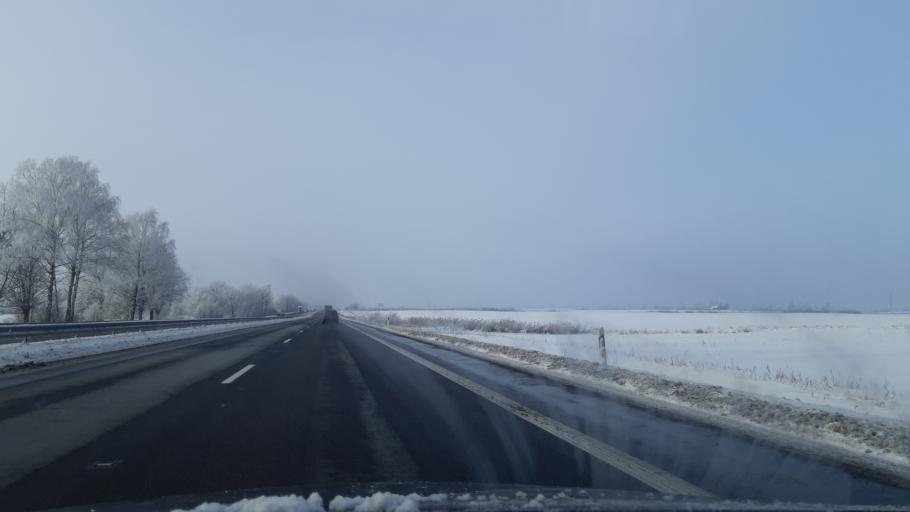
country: LT
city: Kaisiadorys
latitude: 54.8622
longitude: 24.2650
